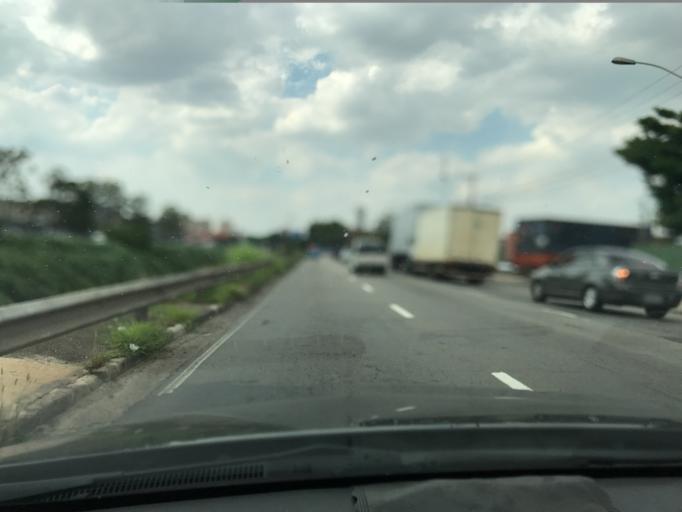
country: BR
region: Sao Paulo
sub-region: Sao Caetano Do Sul
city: Sao Caetano do Sul
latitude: -23.6140
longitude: -46.5436
